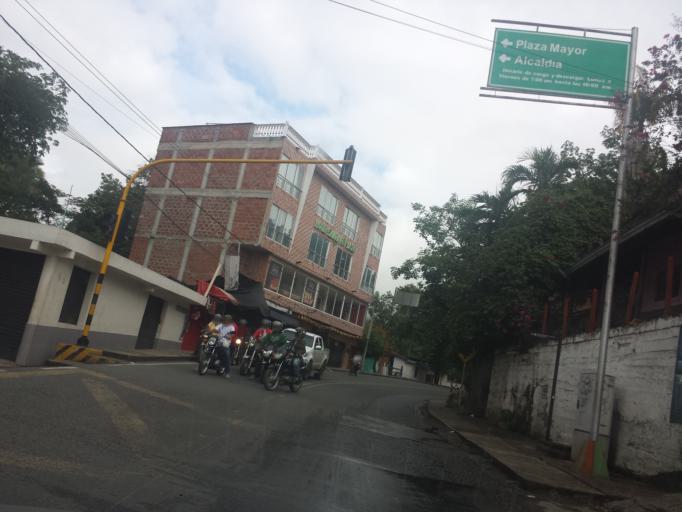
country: CO
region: Antioquia
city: Antioquia
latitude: 6.5590
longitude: -75.8268
